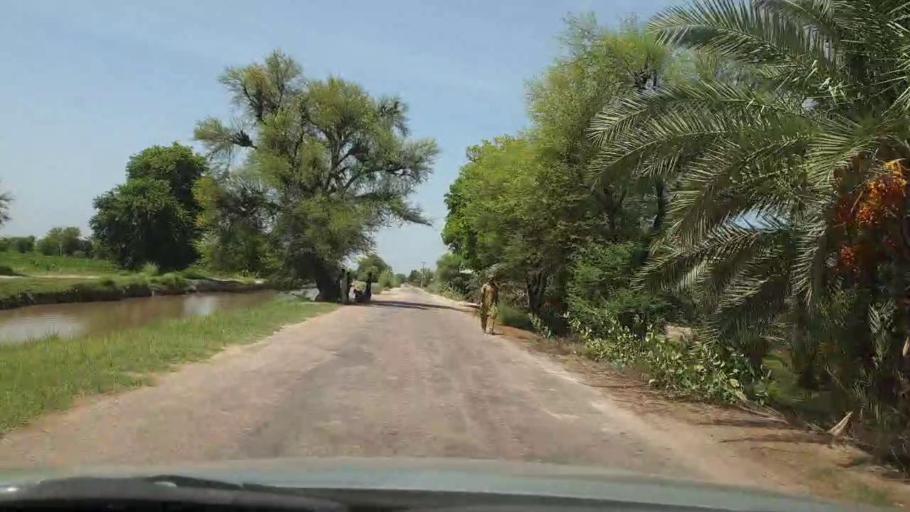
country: PK
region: Sindh
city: Pano Aqil
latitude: 27.6804
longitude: 69.1098
